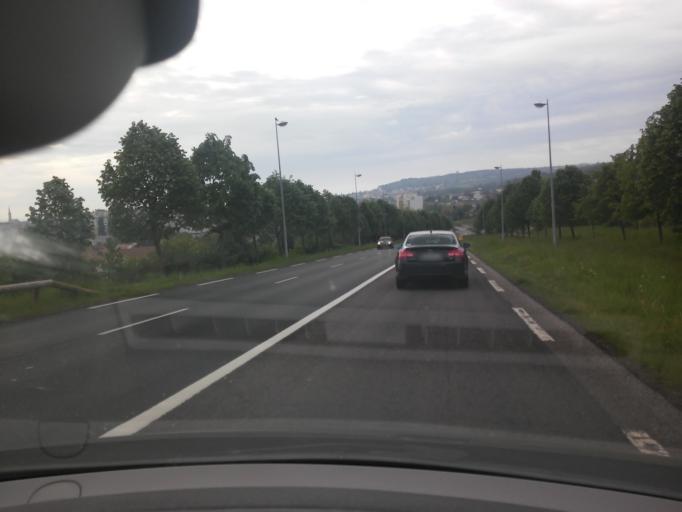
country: FR
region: Lorraine
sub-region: Departement de Meurthe-et-Moselle
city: Laxou
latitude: 48.6829
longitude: 6.1399
